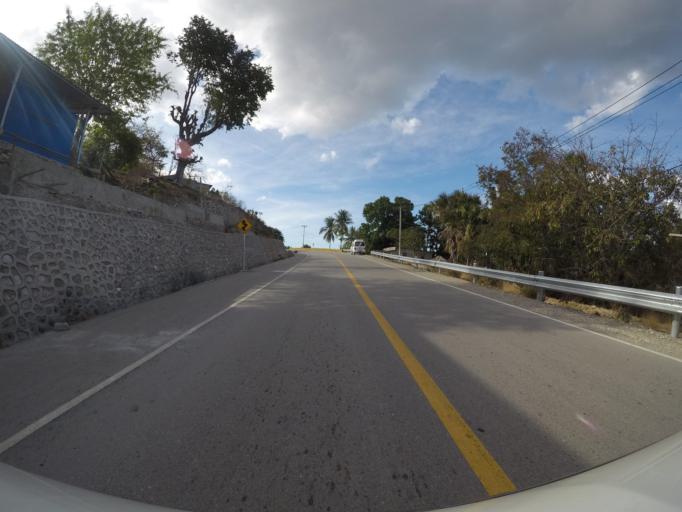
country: TL
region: Baucau
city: Baucau
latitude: -8.4677
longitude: 126.4845
